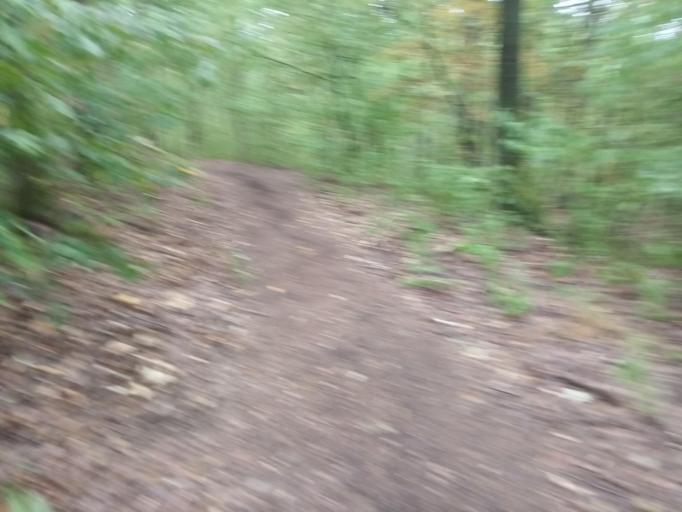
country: HU
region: Pest
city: Csobanka
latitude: 47.6399
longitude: 18.9739
